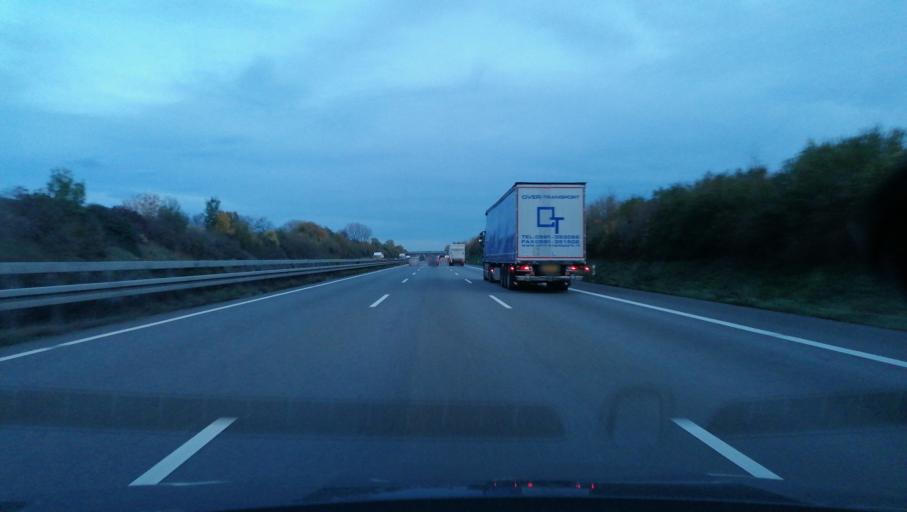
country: DE
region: North Rhine-Westphalia
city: Waltrop
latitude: 51.5799
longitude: 7.4433
